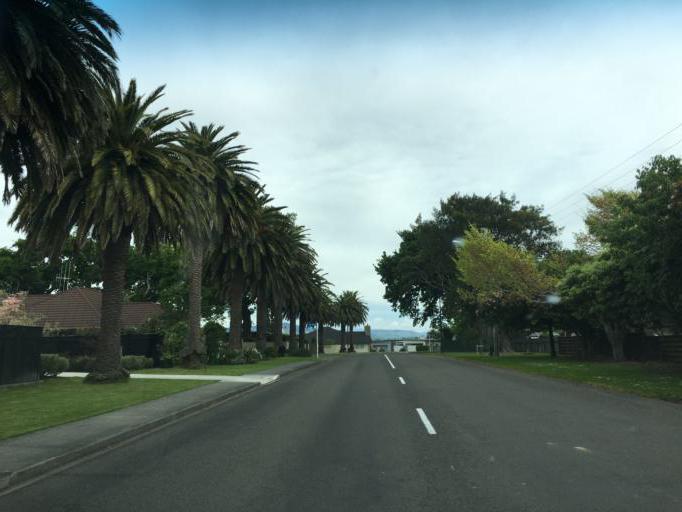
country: NZ
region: Manawatu-Wanganui
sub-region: Palmerston North City
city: Palmerston North
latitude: -40.3781
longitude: 175.5785
